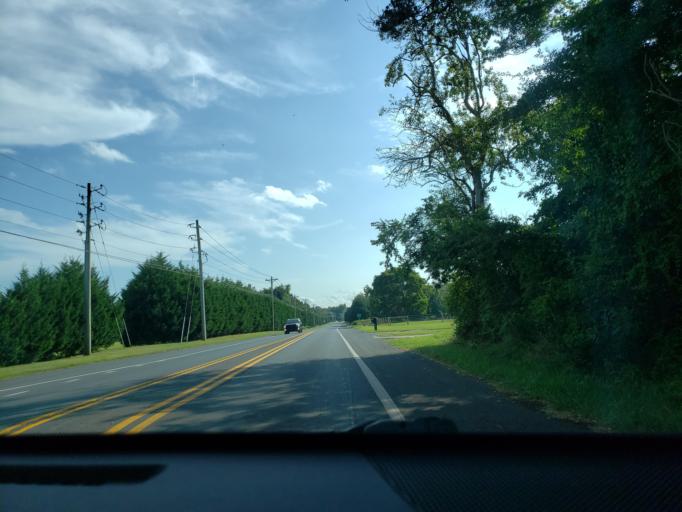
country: US
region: Delaware
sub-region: Sussex County
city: Lewes
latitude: 38.7646
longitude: -75.2183
